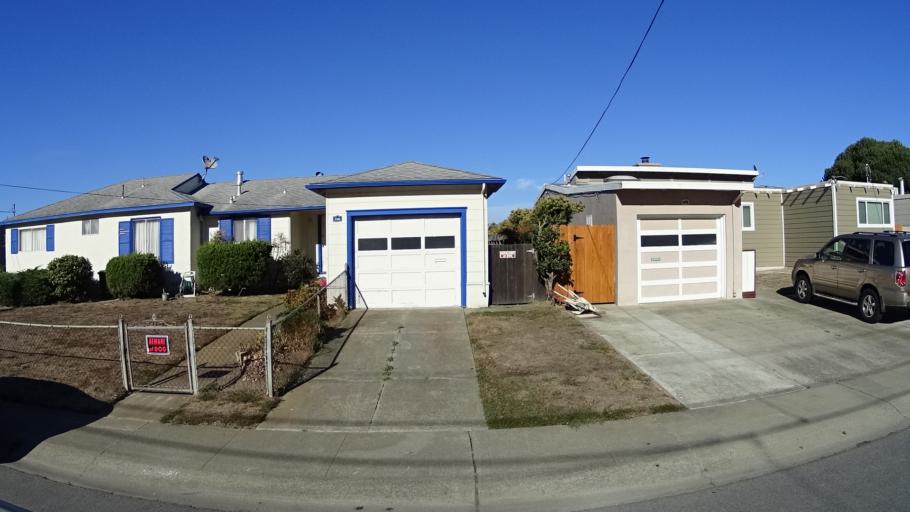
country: US
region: California
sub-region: San Mateo County
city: Broadmoor
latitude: 37.6909
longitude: -122.4852
